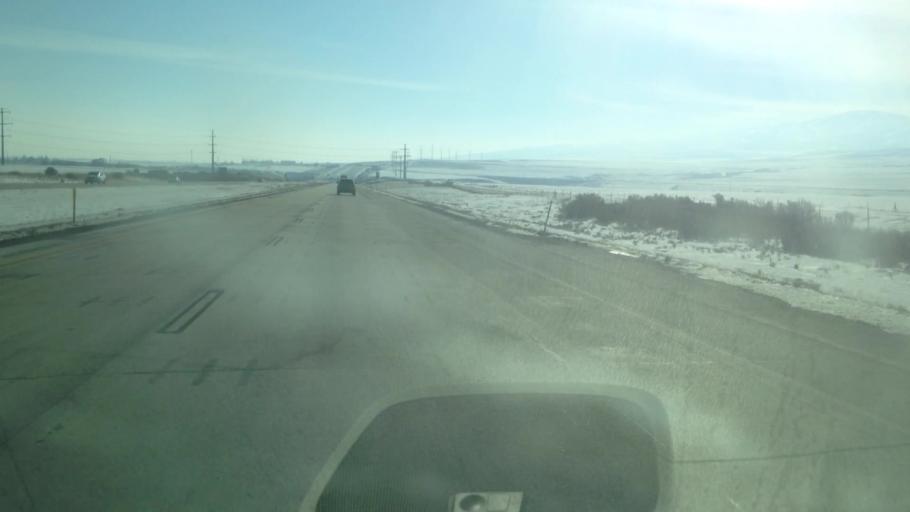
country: US
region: Utah
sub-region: Box Elder County
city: Garland
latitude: 41.8783
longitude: -112.1706
